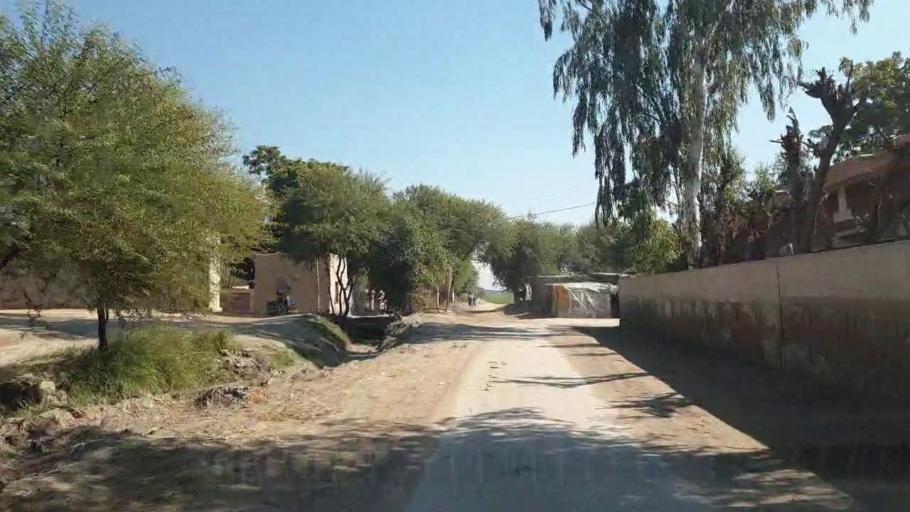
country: PK
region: Sindh
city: Shahpur Chakar
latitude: 26.1079
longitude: 68.6355
